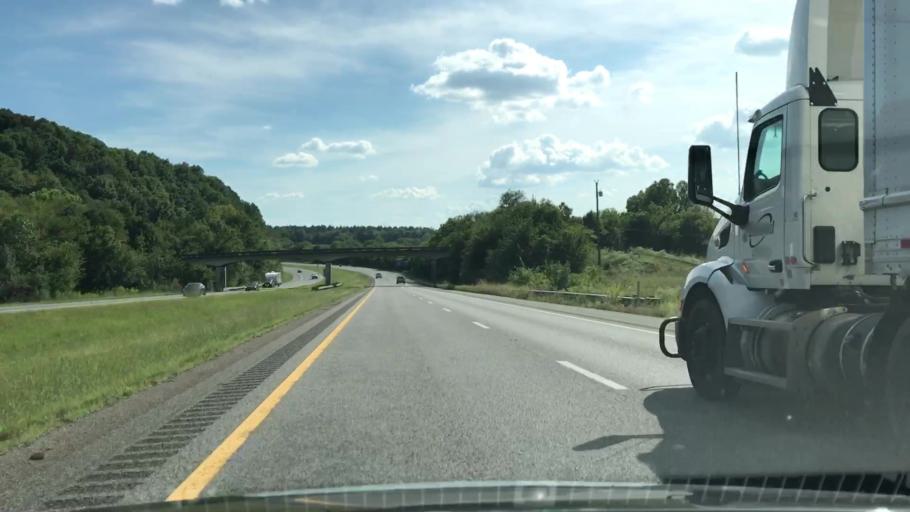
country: US
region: Alabama
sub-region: Limestone County
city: Ardmore
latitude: 35.1095
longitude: -86.8839
